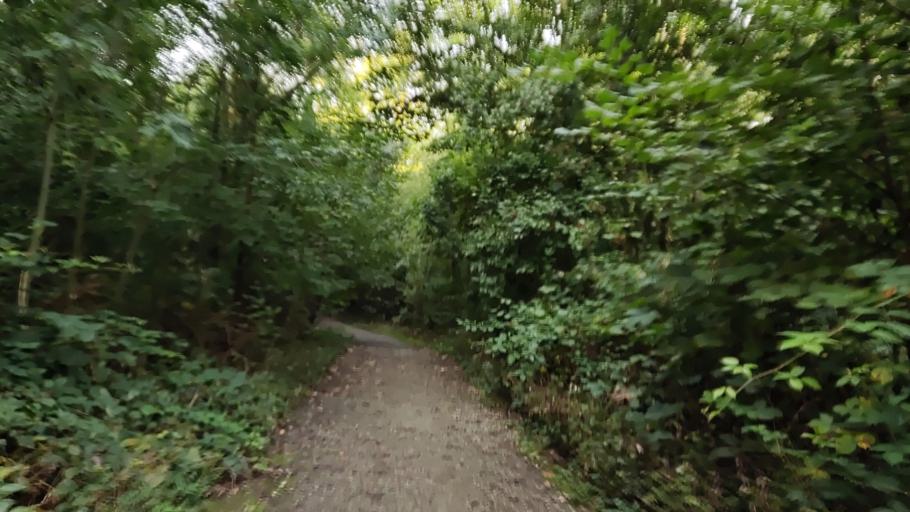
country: DE
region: North Rhine-Westphalia
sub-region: Regierungsbezirk Arnsberg
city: Herne
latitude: 51.5431
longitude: 7.2419
